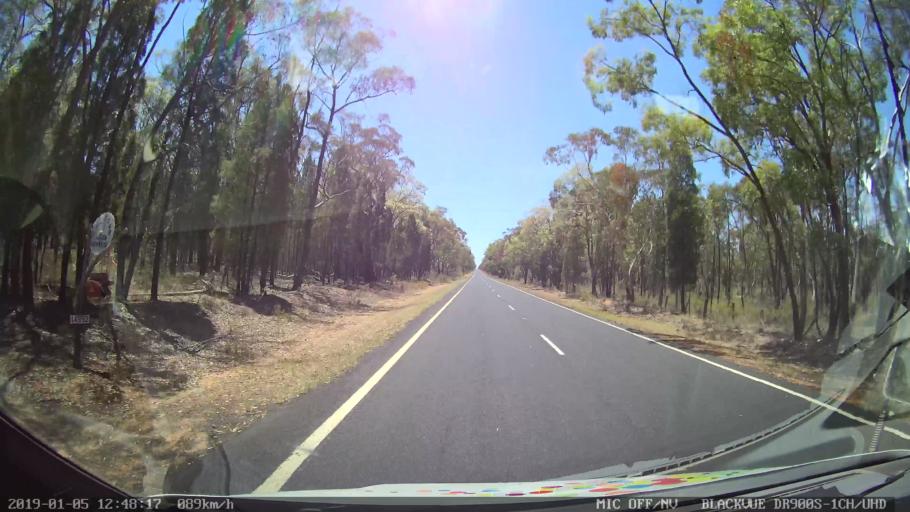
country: AU
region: New South Wales
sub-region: Warrumbungle Shire
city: Coonabarabran
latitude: -31.1181
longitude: 149.5895
